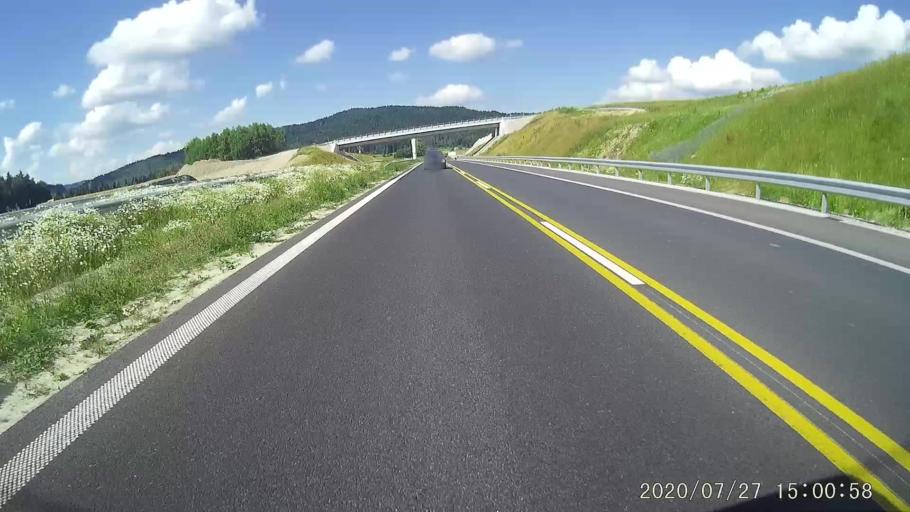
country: PL
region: Lesser Poland Voivodeship
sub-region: Powiat suski
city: Letownia
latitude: 49.6876
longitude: 19.8965
